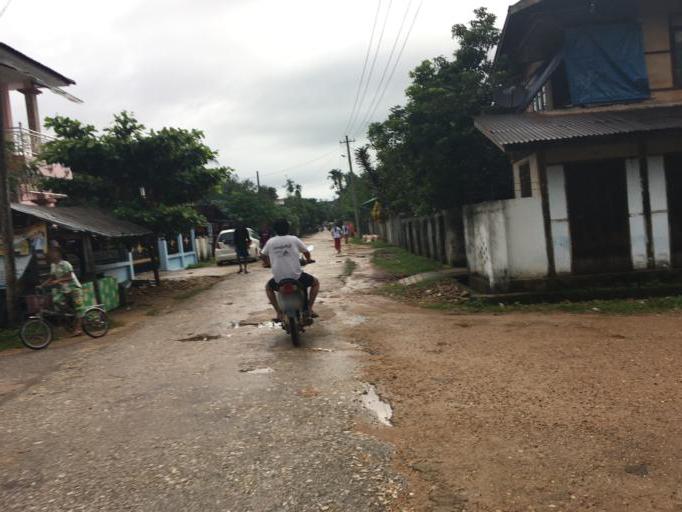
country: MM
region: Mon
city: Mudon
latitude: 16.0402
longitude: 98.1189
